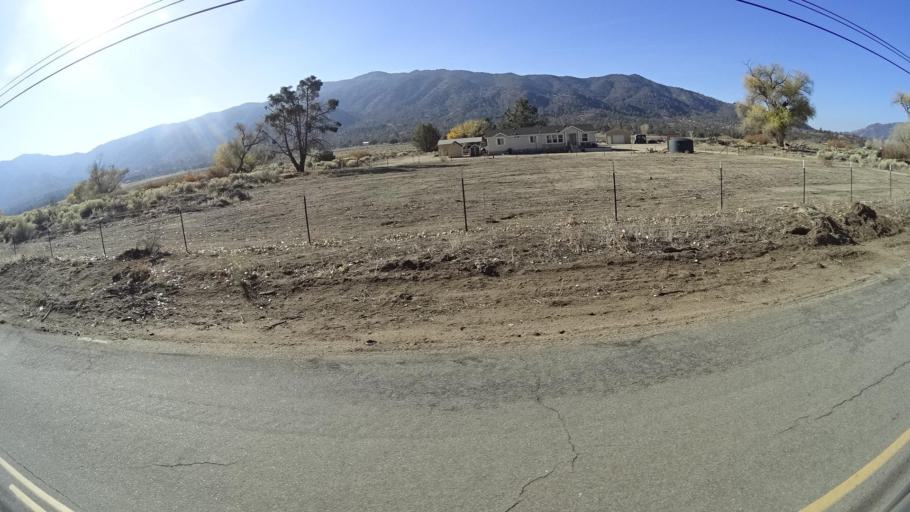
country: US
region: California
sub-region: Kern County
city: Bodfish
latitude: 35.4042
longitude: -118.4853
